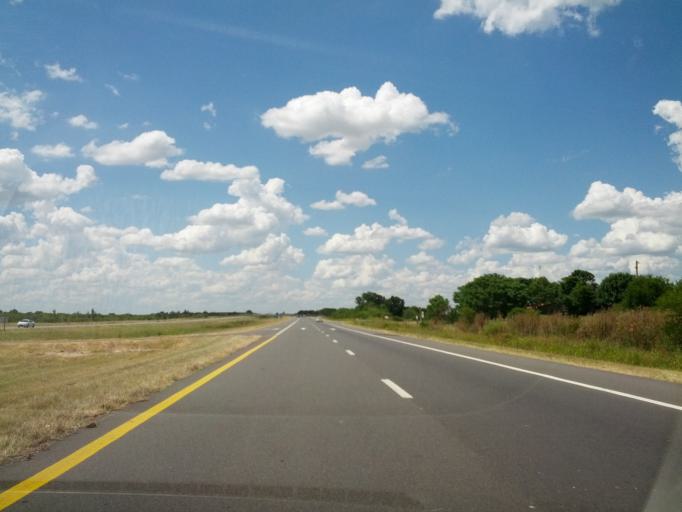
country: AR
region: Entre Rios
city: Colonia Elia
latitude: -32.7469
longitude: -58.4798
